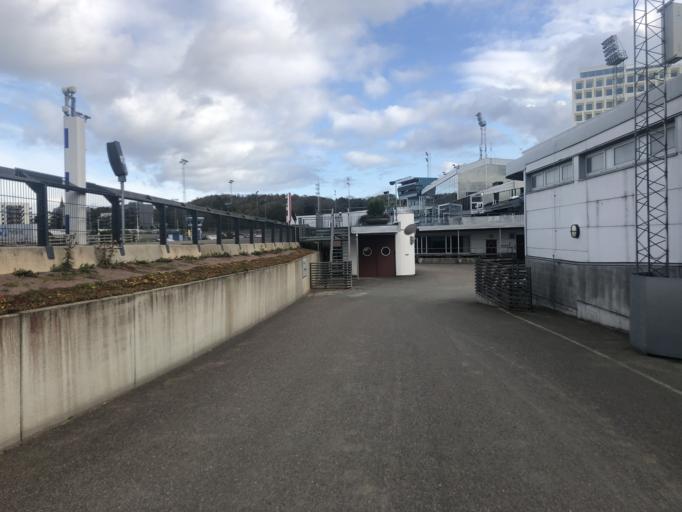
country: SE
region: Vaestra Goetaland
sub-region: Molndal
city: Moelndal
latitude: 57.6494
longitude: 12.0000
